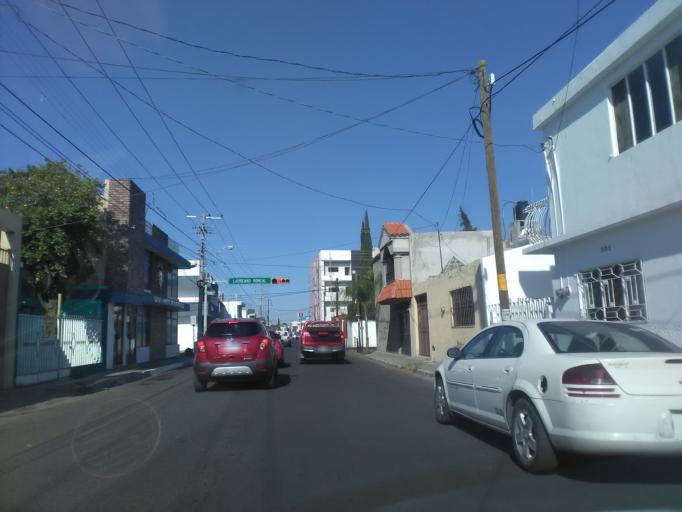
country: MX
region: Durango
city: Victoria de Durango
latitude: 24.0325
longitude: -104.6597
